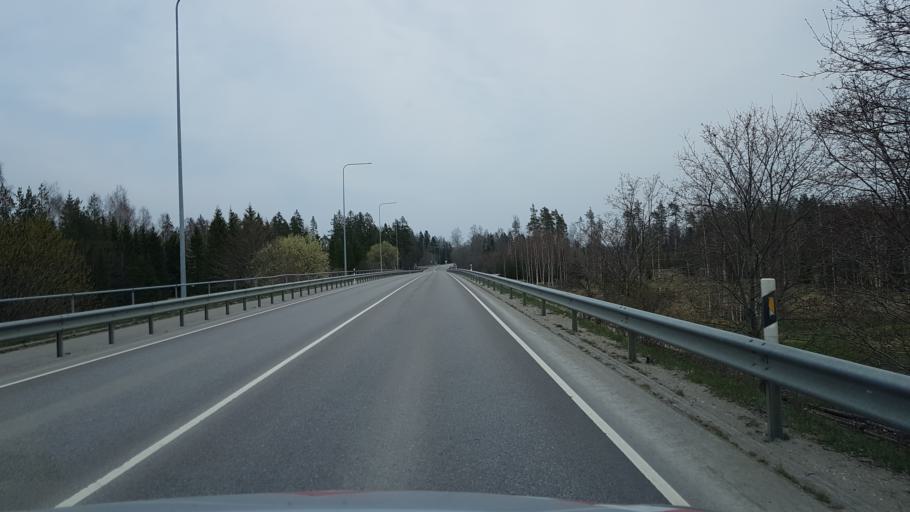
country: EE
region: Laeaene-Virumaa
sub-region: Someru vald
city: Someru
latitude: 59.3595
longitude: 26.4093
